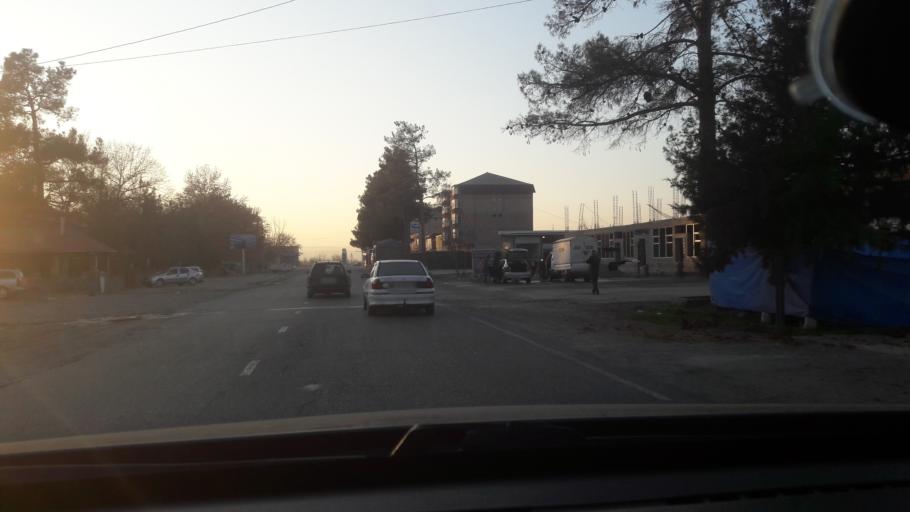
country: TJ
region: Khatlon
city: Vose'
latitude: 37.8052
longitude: 69.6238
